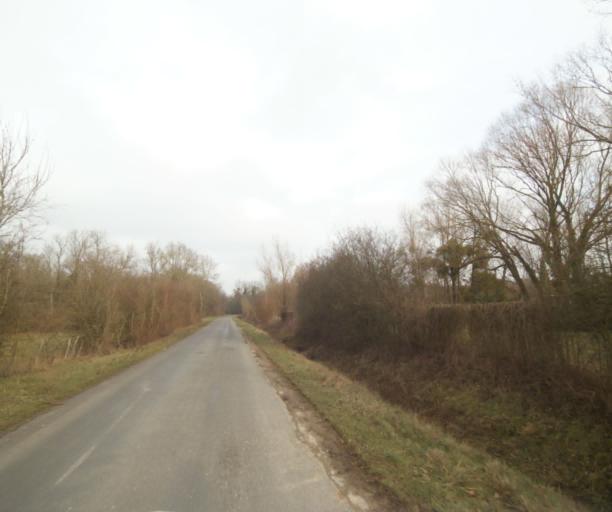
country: FR
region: Champagne-Ardenne
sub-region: Departement de la Haute-Marne
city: Villiers-en-Lieu
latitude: 48.6631
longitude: 4.8320
